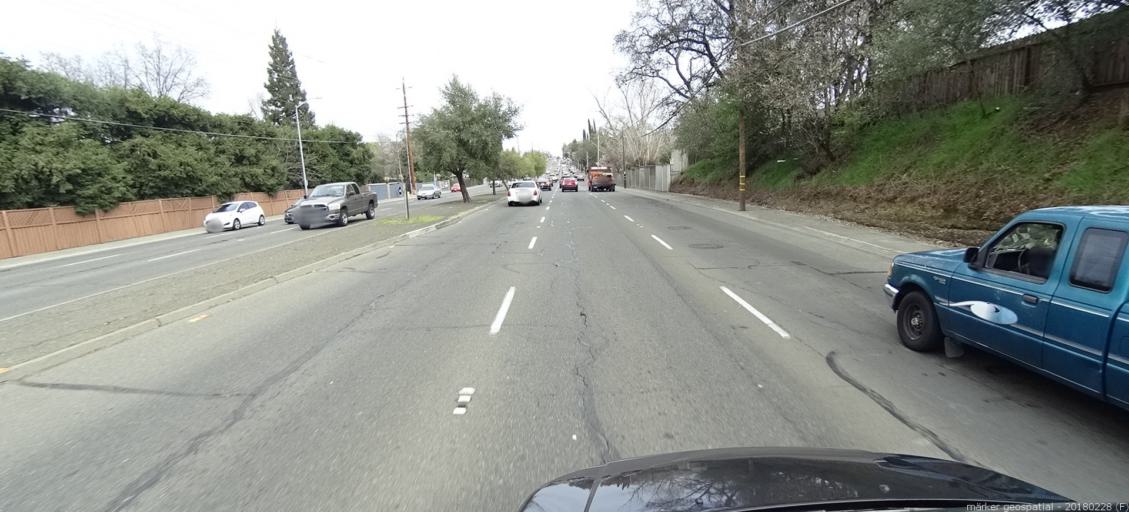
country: US
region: California
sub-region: Sacramento County
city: Fair Oaks
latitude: 38.6635
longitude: -121.2992
